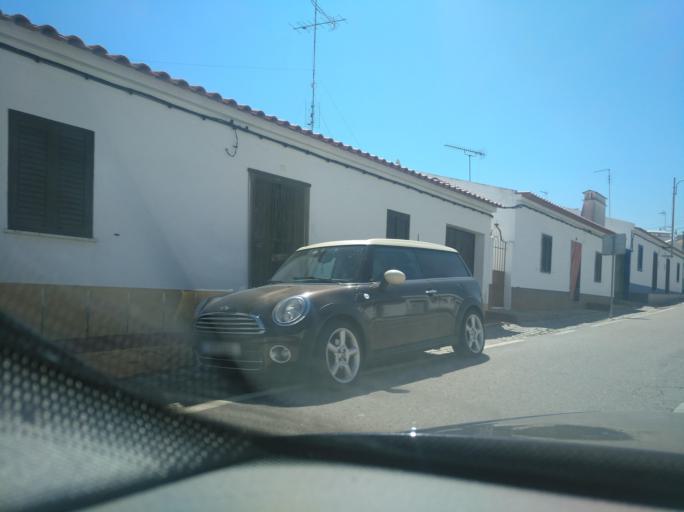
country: PT
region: Portalegre
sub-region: Elvas
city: Elvas
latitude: 38.9620
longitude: -7.2988
